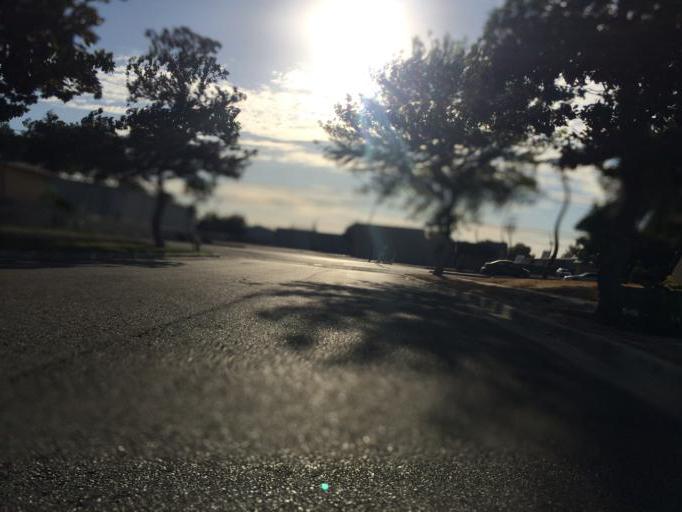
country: US
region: California
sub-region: Fresno County
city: Sunnyside
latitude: 36.7628
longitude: -119.7357
